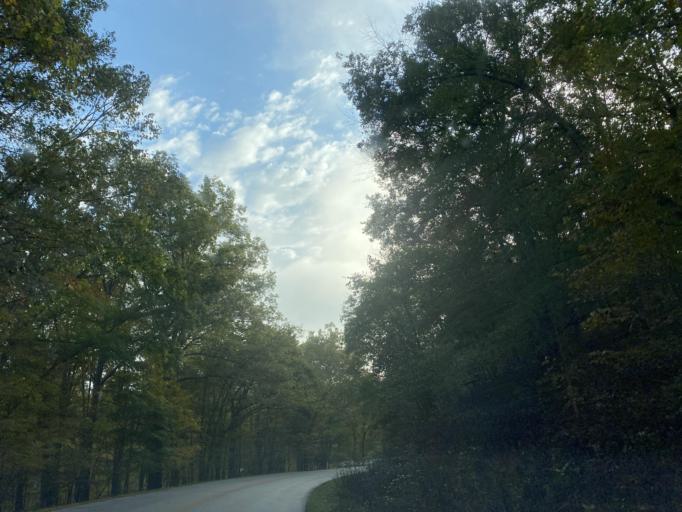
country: US
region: Kentucky
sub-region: Pendleton County
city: Falmouth
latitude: 38.7222
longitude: -84.2854
